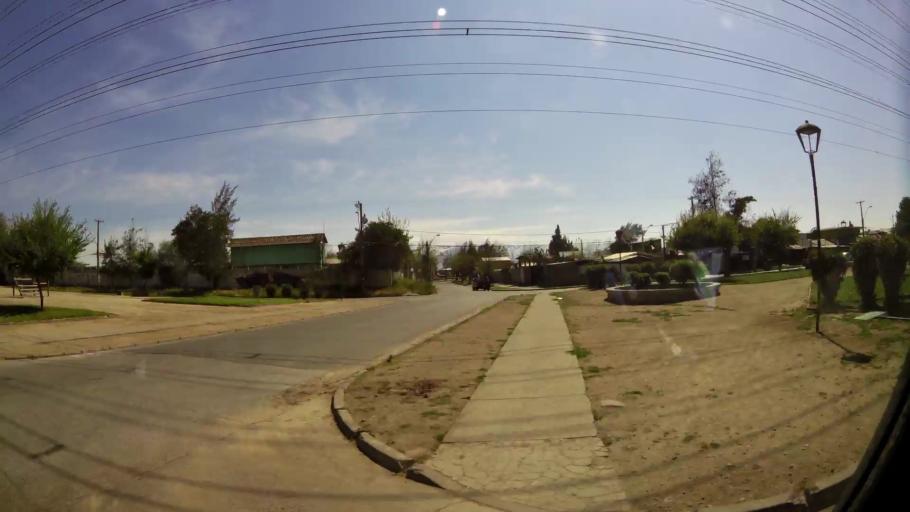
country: CL
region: Santiago Metropolitan
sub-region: Provincia de Santiago
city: Lo Prado
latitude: -33.5001
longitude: -70.7331
